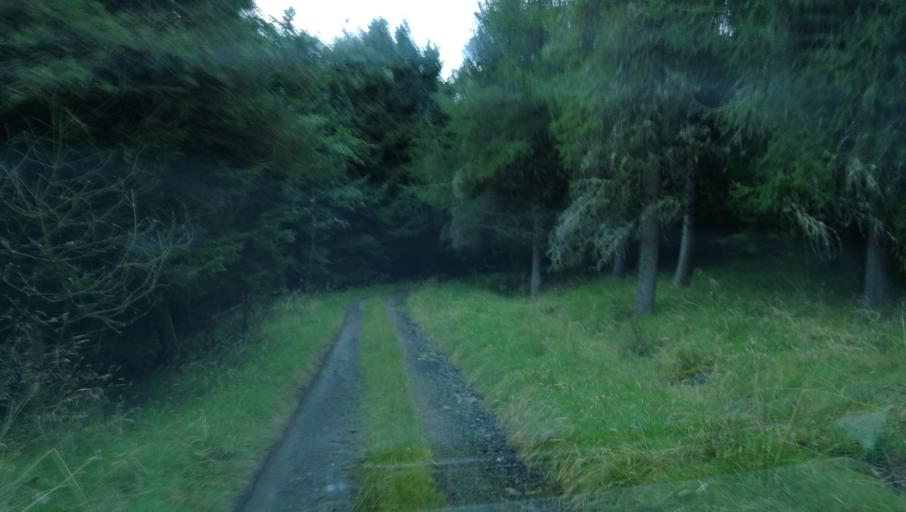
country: GB
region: Scotland
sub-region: Perth and Kinross
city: Blairgowrie
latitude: 56.6688
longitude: -3.3474
